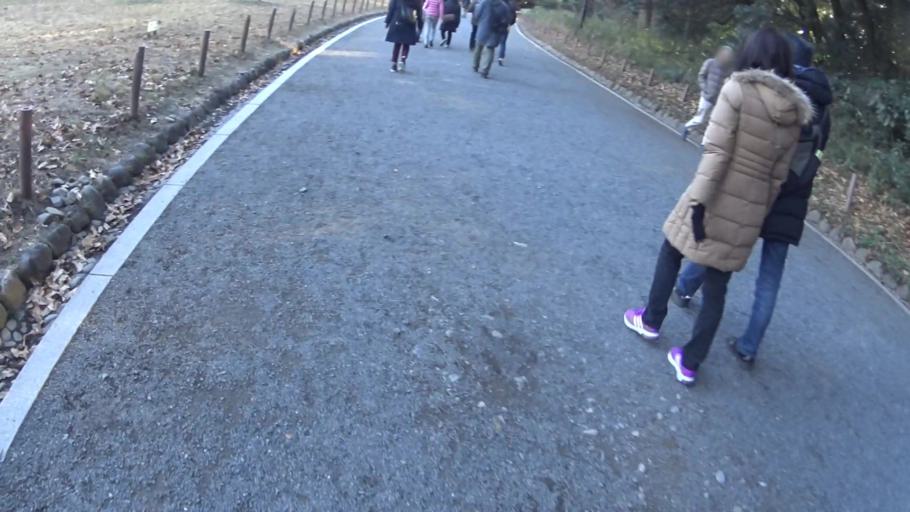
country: JP
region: Tokyo
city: Tokyo
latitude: 35.6786
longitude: 139.6959
